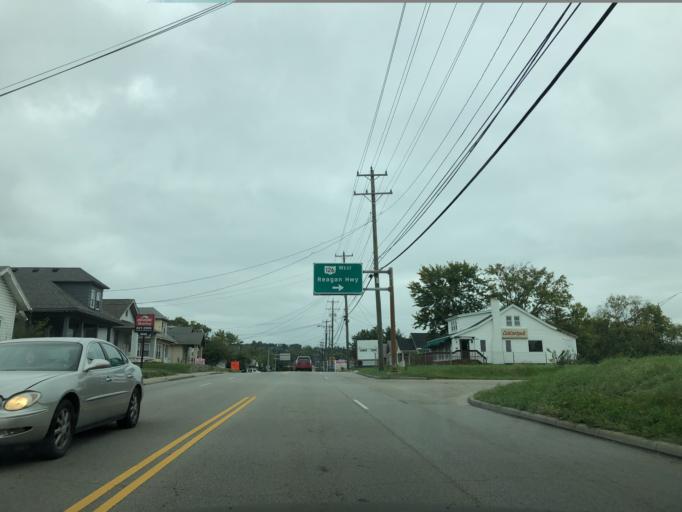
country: US
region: Ohio
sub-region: Hamilton County
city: Reading
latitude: 39.2118
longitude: -84.4516
